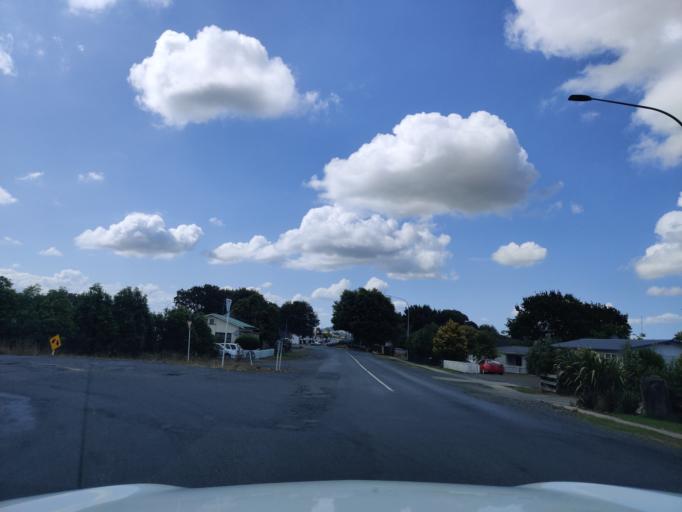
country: NZ
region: Auckland
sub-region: Auckland
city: Pukekohe East
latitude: -37.2439
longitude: 175.0187
